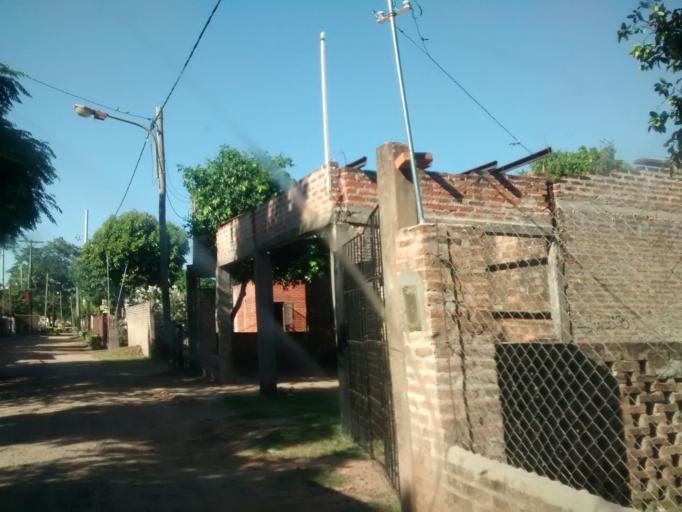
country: AR
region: Chaco
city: Resistencia
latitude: -27.4270
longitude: -58.9839
